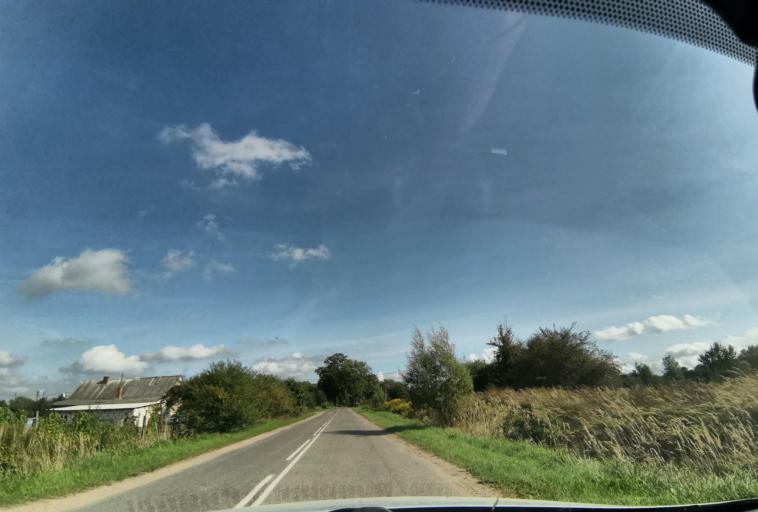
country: RU
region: Kaliningrad
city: Chernyakhovsk
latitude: 54.6514
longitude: 21.8474
